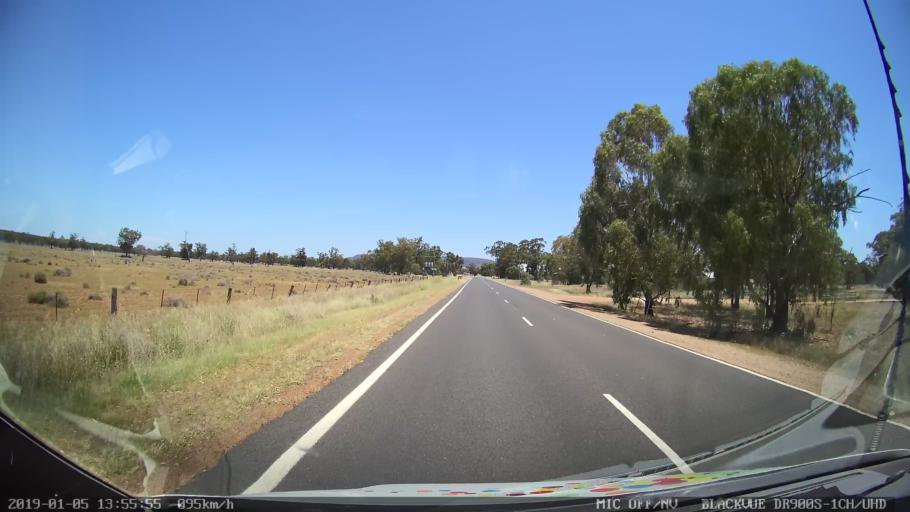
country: AU
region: New South Wales
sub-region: Gunnedah
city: Gunnedah
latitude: -31.1098
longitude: 150.2698
